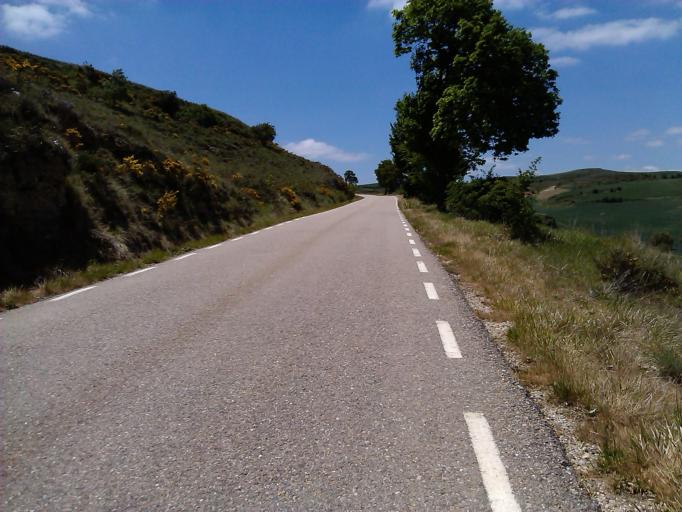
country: ES
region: Castille and Leon
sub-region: Provincia de Burgos
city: Cerraton de Juarros
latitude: 42.4293
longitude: -3.3599
